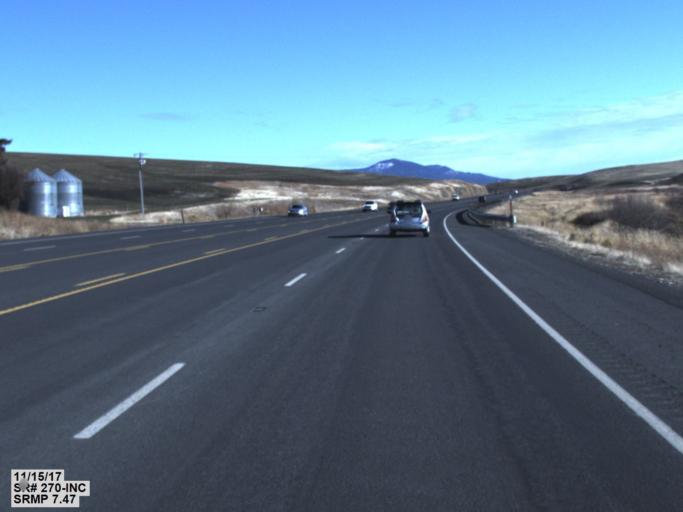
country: US
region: Idaho
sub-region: Latah County
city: Moscow
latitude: 46.7323
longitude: -117.0860
